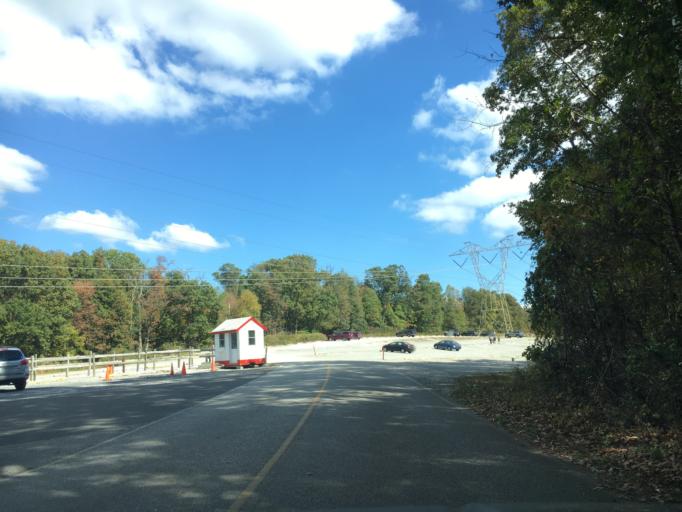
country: US
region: Pennsylvania
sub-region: York County
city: Yorklyn
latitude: 40.0117
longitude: -76.6515
